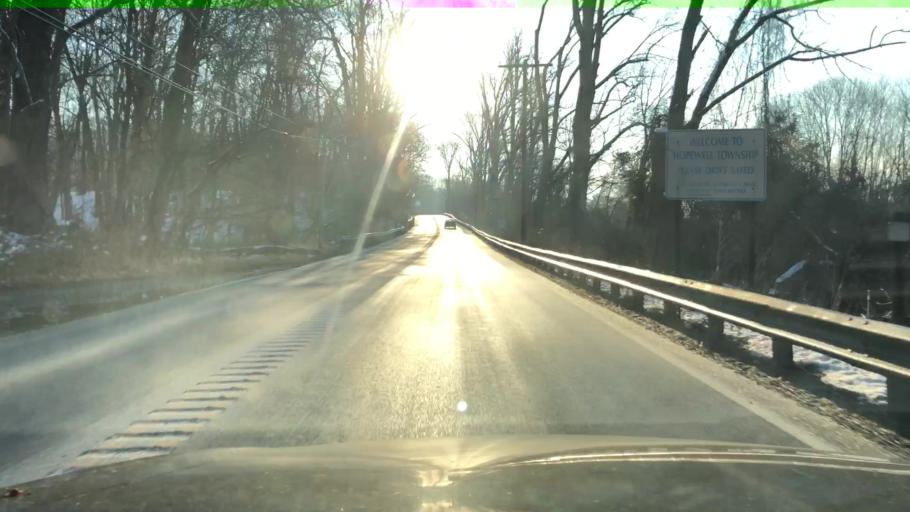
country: US
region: New Jersey
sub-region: Hunterdon County
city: Lambertville
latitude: 40.3379
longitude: -74.9320
